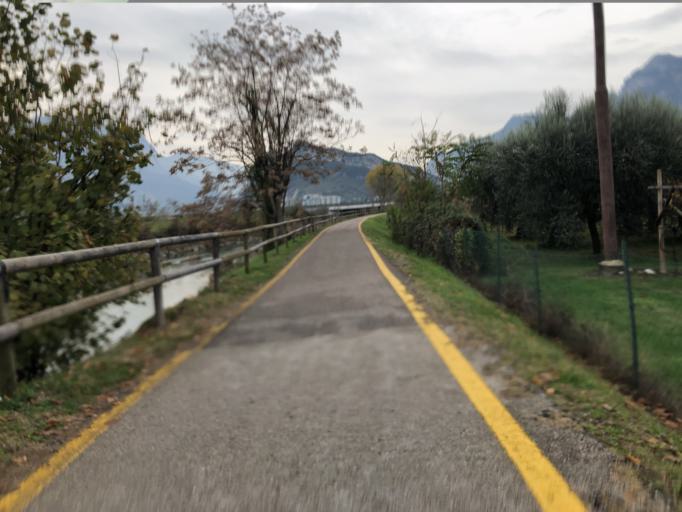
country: IT
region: Trentino-Alto Adige
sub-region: Provincia di Trento
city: Arco
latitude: 45.9115
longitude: 10.8840
